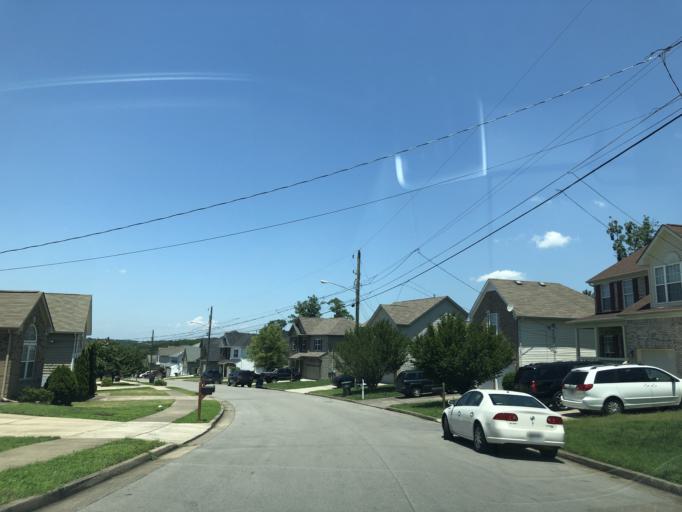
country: US
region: Tennessee
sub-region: Rutherford County
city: La Vergne
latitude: 36.0186
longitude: -86.6507
